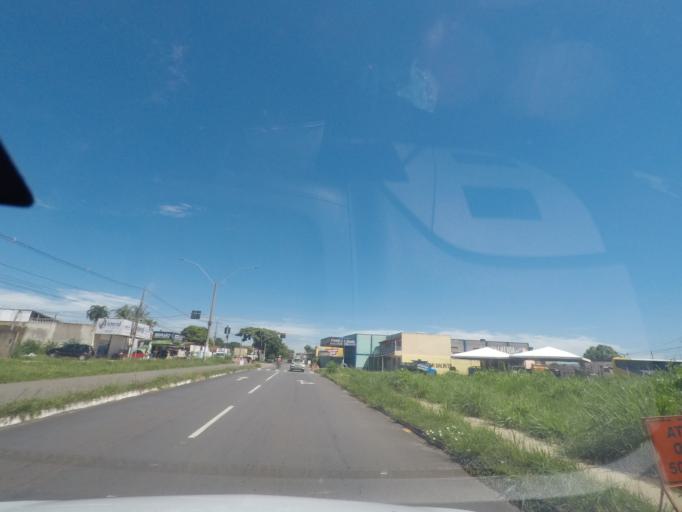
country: BR
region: Goias
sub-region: Aparecida De Goiania
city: Aparecida de Goiania
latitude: -16.7742
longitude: -49.3385
